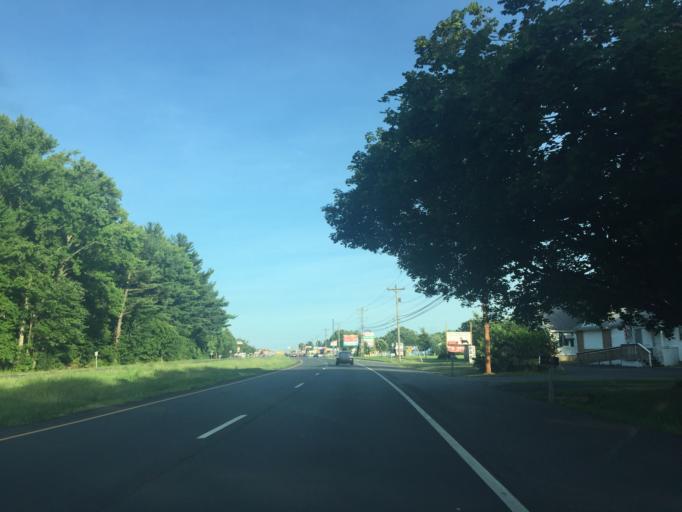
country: US
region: Delaware
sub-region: Kent County
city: Cheswold
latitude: 39.2102
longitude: -75.5700
